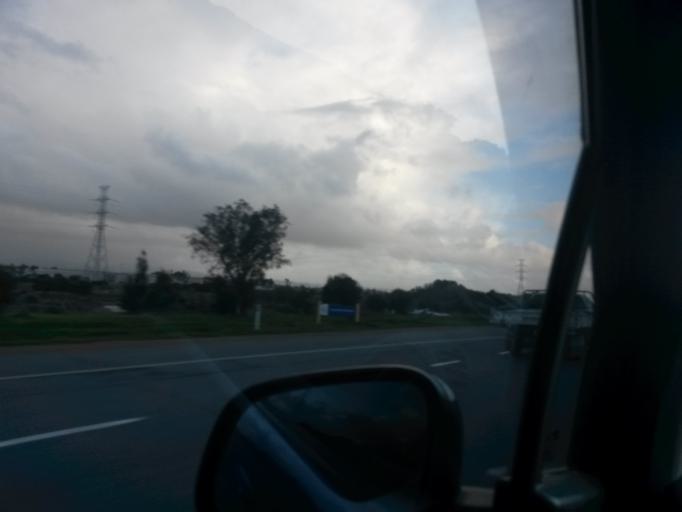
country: AU
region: South Australia
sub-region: Port Adelaide Enfield
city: Enfield
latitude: -34.8229
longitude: 138.5873
